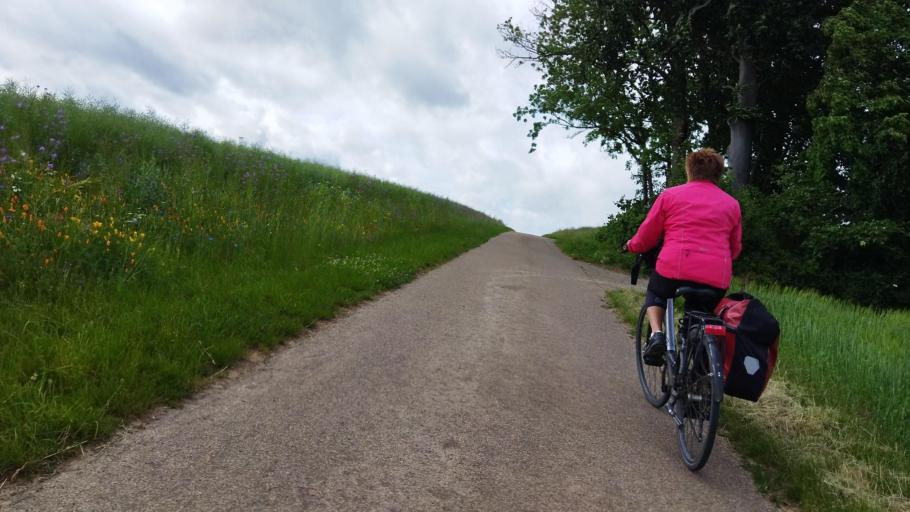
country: DE
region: Baden-Wuerttemberg
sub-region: Regierungsbezirk Stuttgart
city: Leingarten
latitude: 49.1659
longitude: 9.1273
